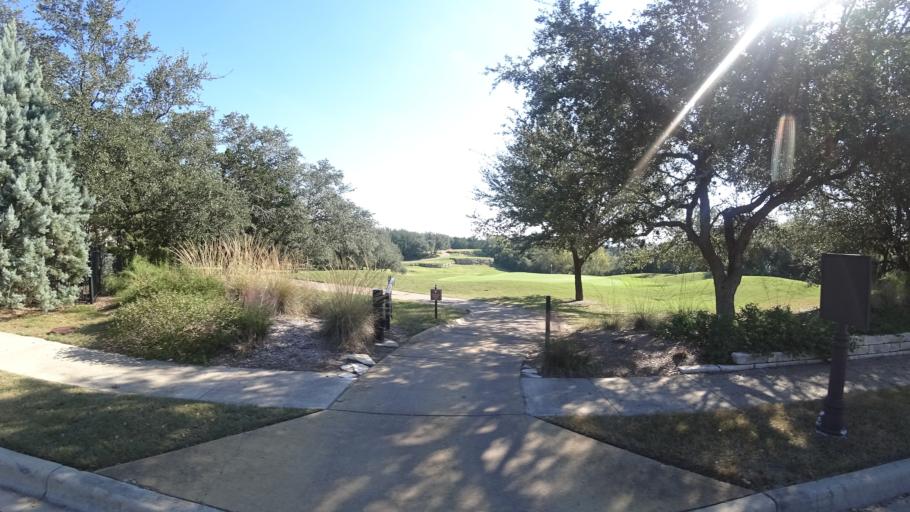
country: US
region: Texas
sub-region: Travis County
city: Barton Creek
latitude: 30.3527
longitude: -97.8876
